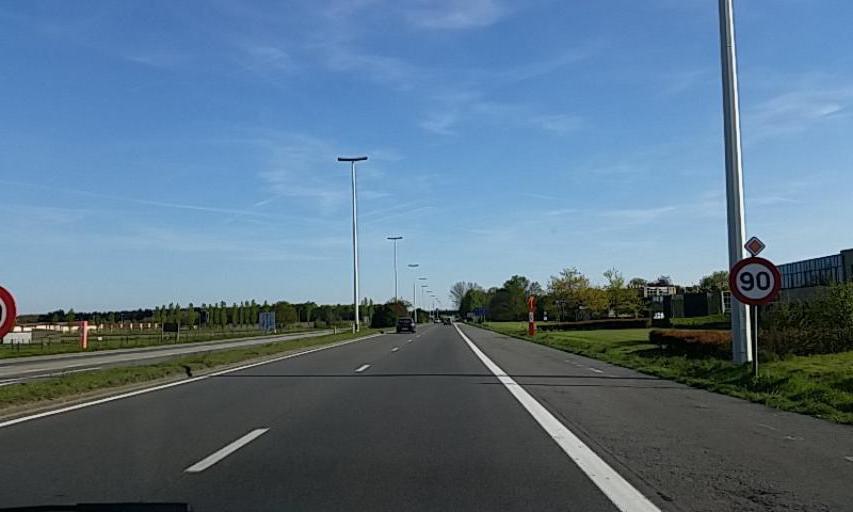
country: BE
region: Flanders
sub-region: Provincie Oost-Vlaanderen
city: Zelzate
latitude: 51.1972
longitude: 3.8281
